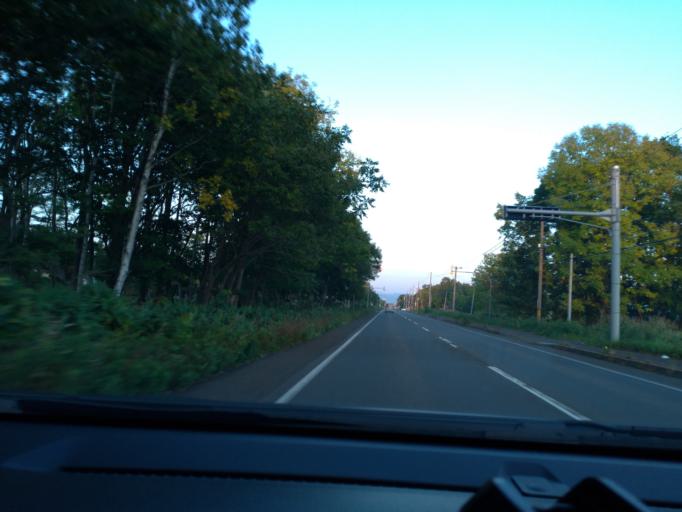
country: JP
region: Hokkaido
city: Tobetsu
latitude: 43.3271
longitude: 141.6386
